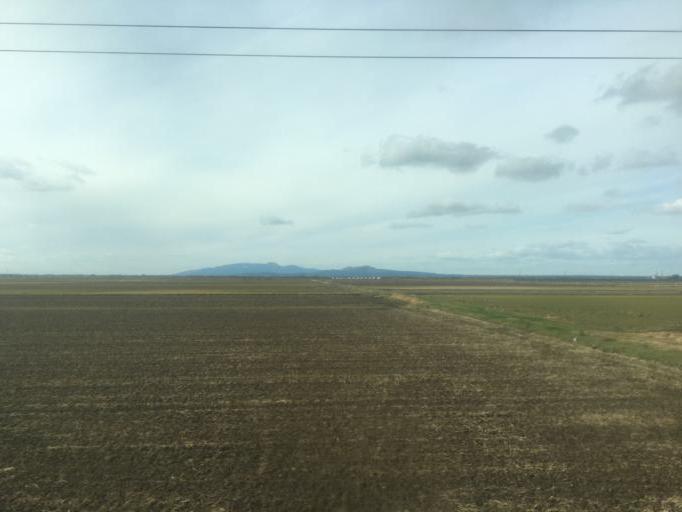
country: JP
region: Akita
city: Tenno
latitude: 39.9097
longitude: 140.0756
